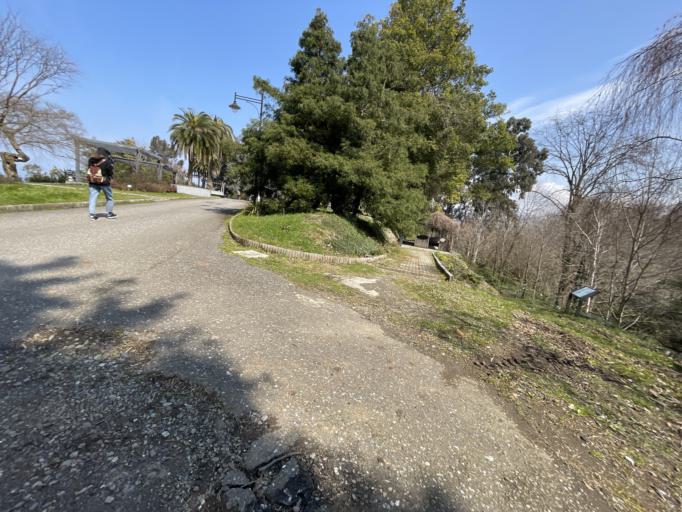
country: GE
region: Ajaria
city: Makhinjauri
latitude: 41.6980
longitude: 41.7167
